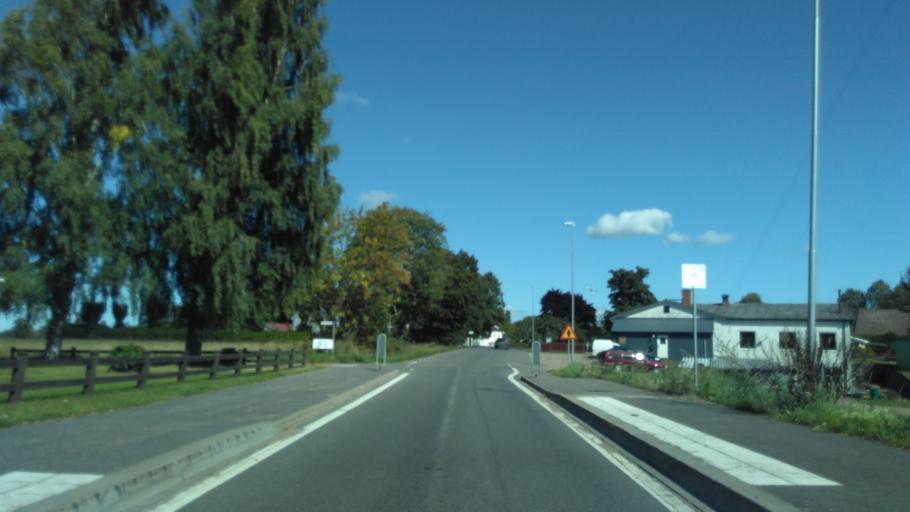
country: SE
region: Vaestra Goetaland
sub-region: Skara Kommun
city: Axvall
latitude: 58.4324
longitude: 13.6416
